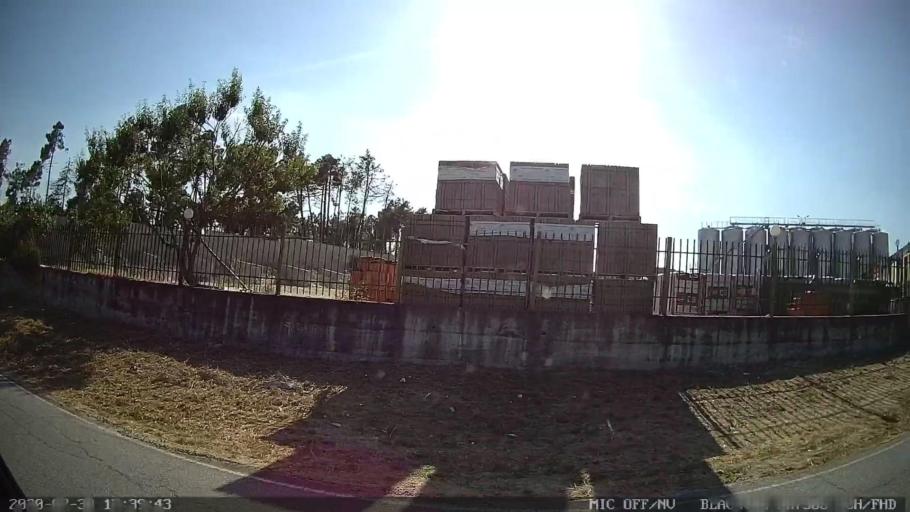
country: PT
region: Vila Real
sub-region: Murca
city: Murca
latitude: 41.3818
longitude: -7.5003
